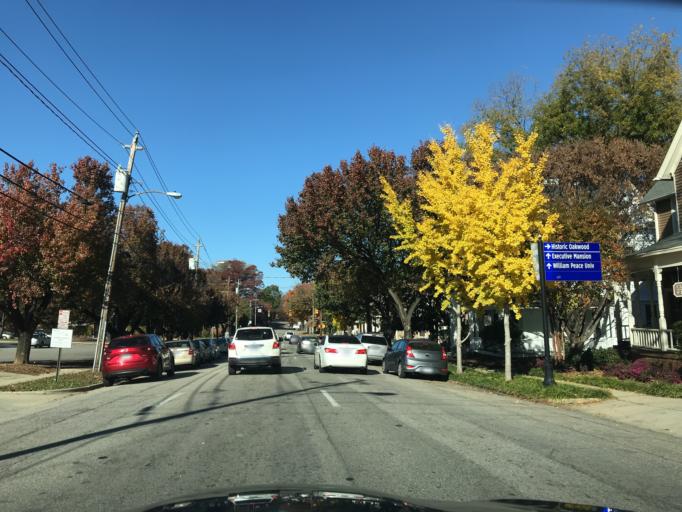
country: US
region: North Carolina
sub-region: Wake County
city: Raleigh
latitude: 35.7815
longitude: -78.6348
